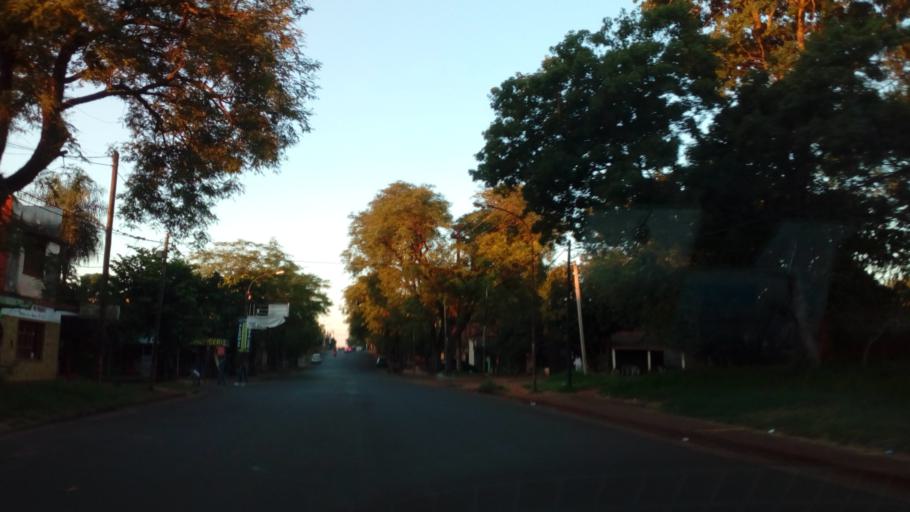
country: AR
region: Misiones
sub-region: Departamento de Capital
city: Posadas
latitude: -27.4037
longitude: -55.8988
